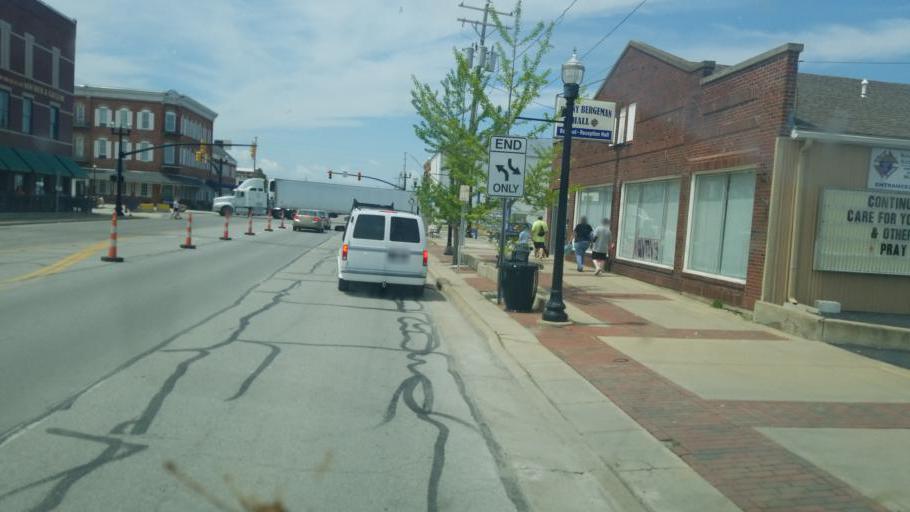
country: US
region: Ohio
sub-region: Ottawa County
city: Port Clinton
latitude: 41.5134
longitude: -82.9403
